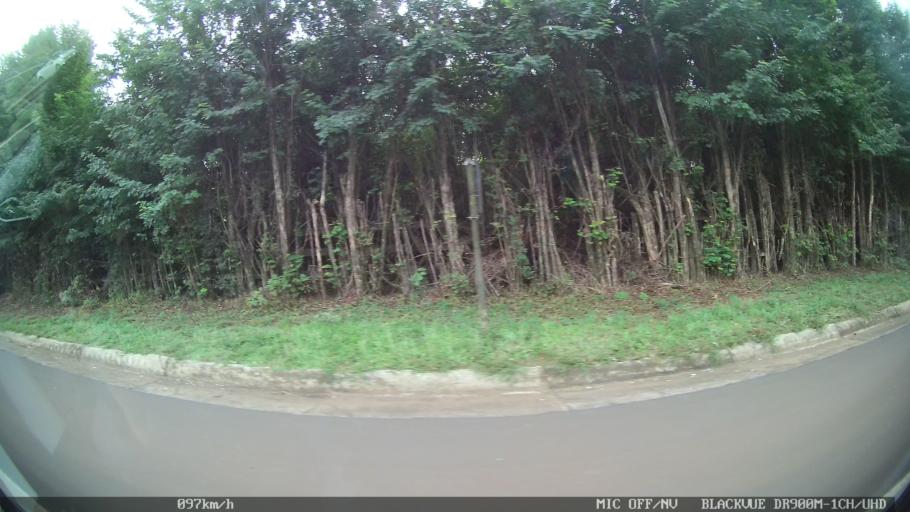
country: BR
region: Sao Paulo
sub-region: Piracicaba
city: Piracicaba
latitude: -22.6988
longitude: -47.5939
